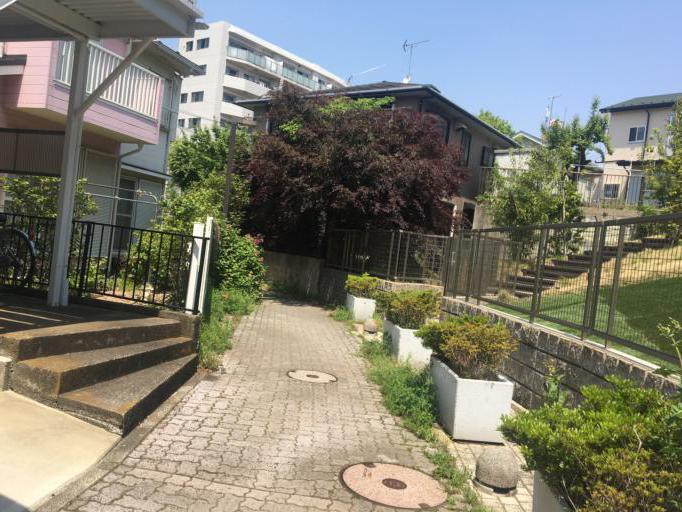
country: JP
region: Saitama
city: Wako
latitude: 35.7741
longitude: 139.6295
